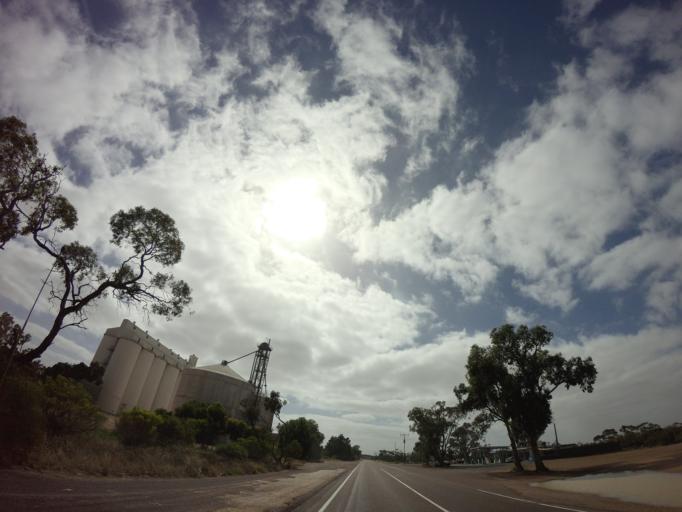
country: AU
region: South Australia
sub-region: Streaky Bay
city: Streaky Bay
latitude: -32.7217
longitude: 134.8366
